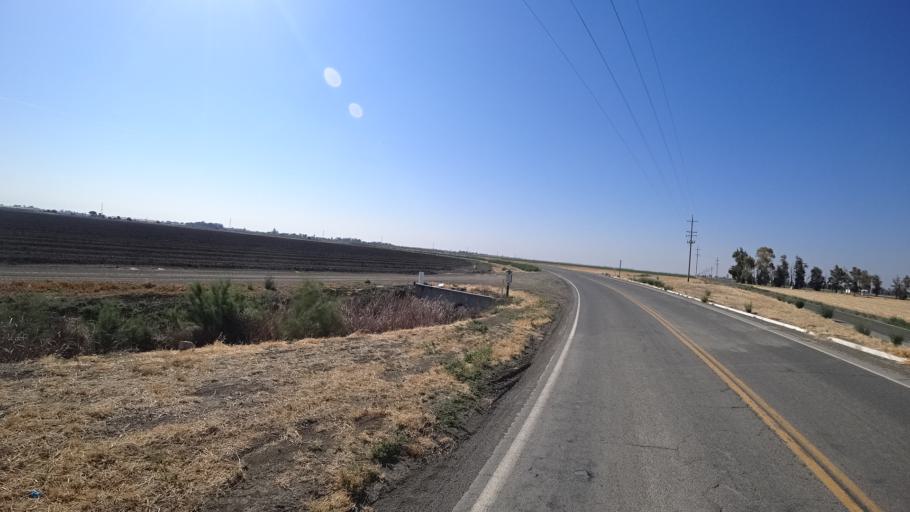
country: US
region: California
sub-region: Kings County
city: Lemoore Station
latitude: 36.3447
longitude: -119.9053
